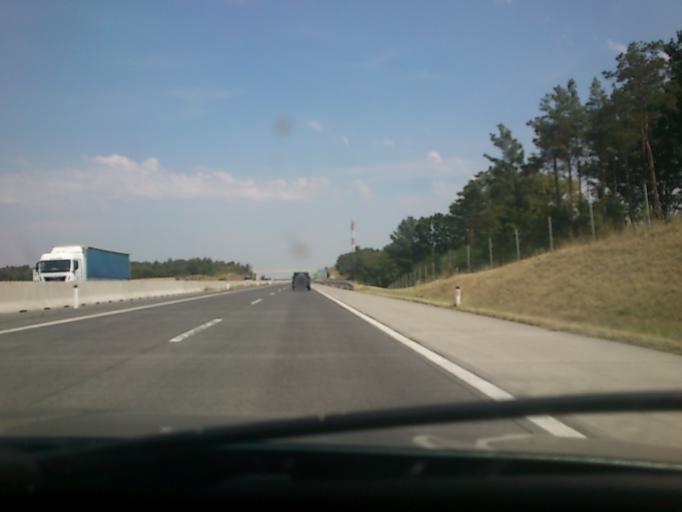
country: AT
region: Lower Austria
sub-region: Politischer Bezirk Mistelbach
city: Wolkersdorf im Weinviertel
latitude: 48.4138
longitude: 16.5397
